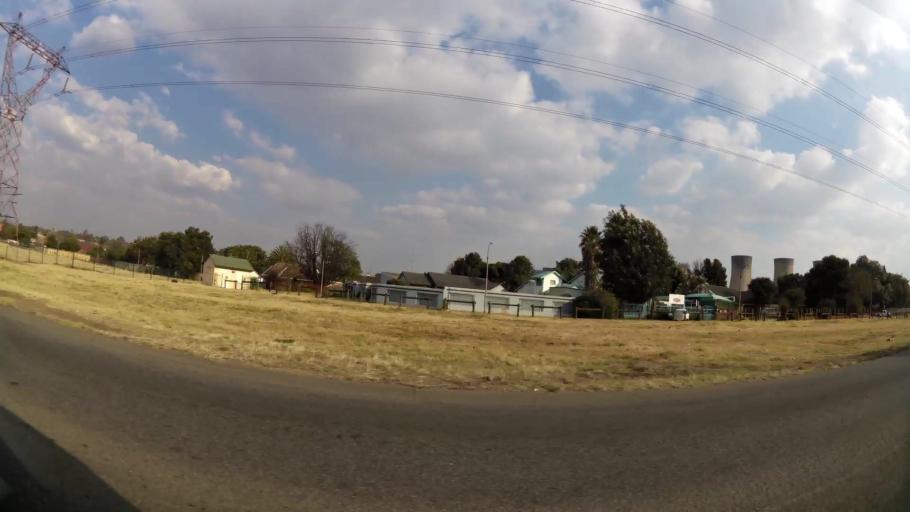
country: ZA
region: Gauteng
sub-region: City of Johannesburg Metropolitan Municipality
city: Modderfontein
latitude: -26.1085
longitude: 28.1994
